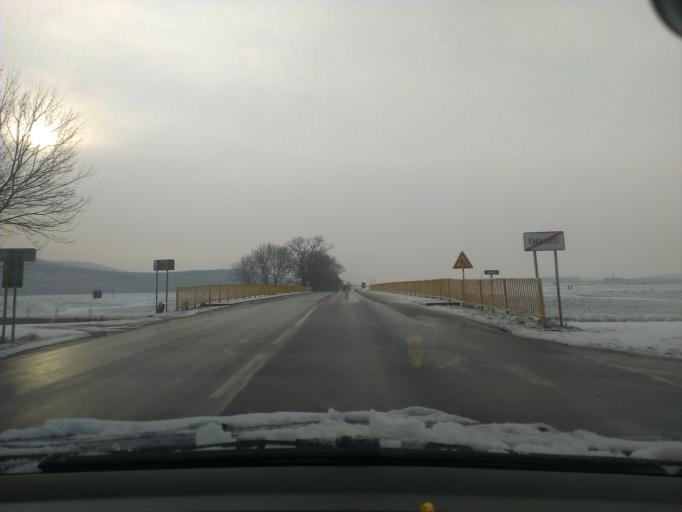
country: SK
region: Nitriansky
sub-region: Okres Nitra
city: Nitra
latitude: 48.3695
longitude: 18.0426
